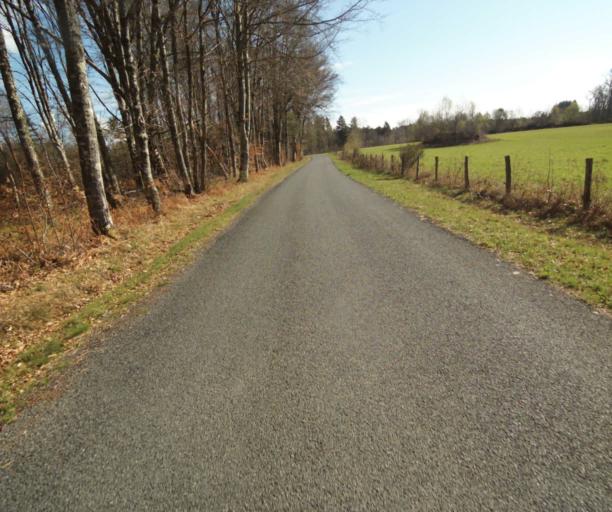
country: FR
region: Limousin
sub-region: Departement de la Correze
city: Correze
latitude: 45.2476
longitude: 1.9217
